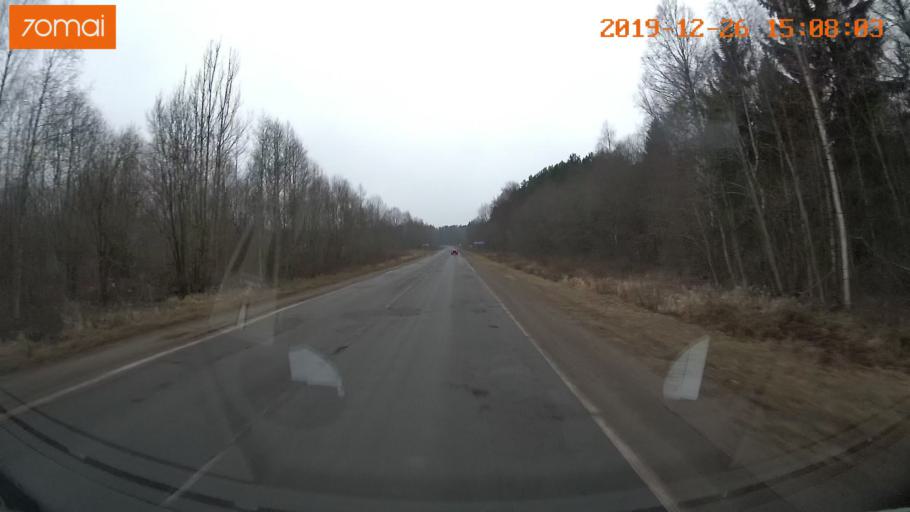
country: RU
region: Jaroslavl
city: Rybinsk
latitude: 58.1637
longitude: 38.8408
